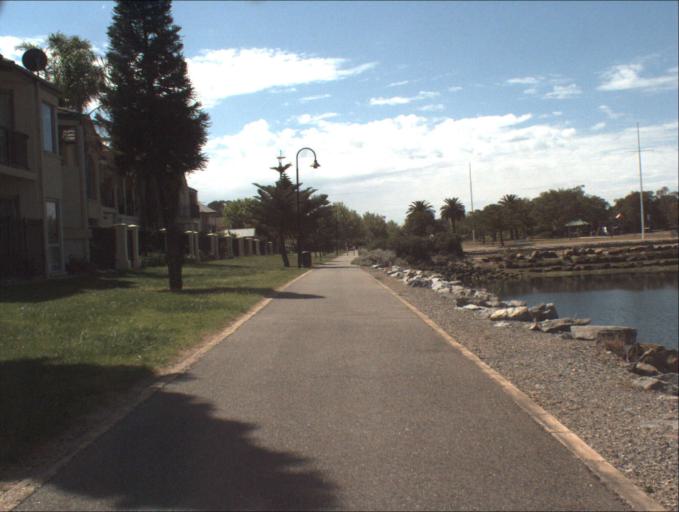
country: AU
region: South Australia
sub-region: Port Adelaide Enfield
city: Birkenhead
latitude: -34.8496
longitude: 138.4991
